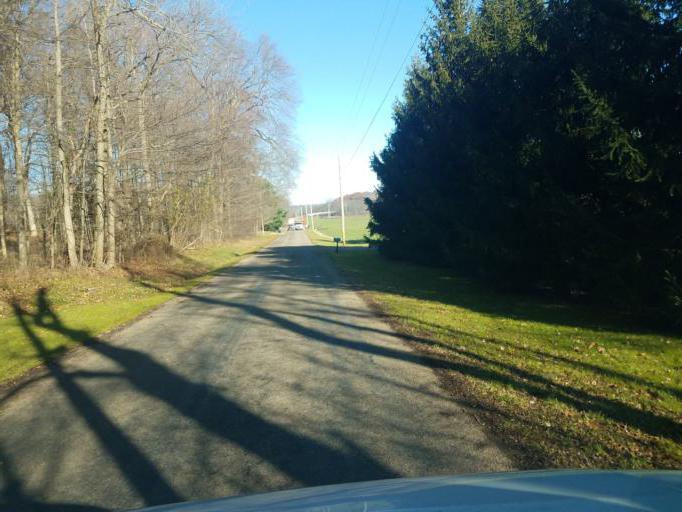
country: US
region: Ohio
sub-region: Richland County
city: Lincoln Heights
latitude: 40.7179
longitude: -82.4464
